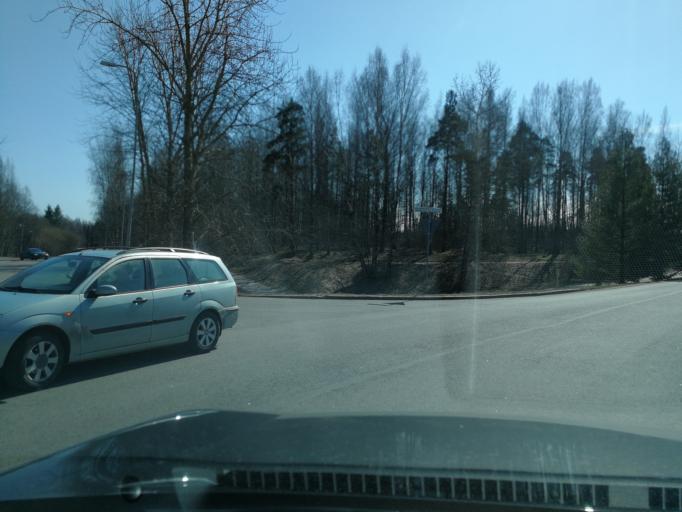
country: FI
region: Uusimaa
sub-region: Helsinki
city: Teekkarikylae
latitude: 60.2452
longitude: 24.8508
